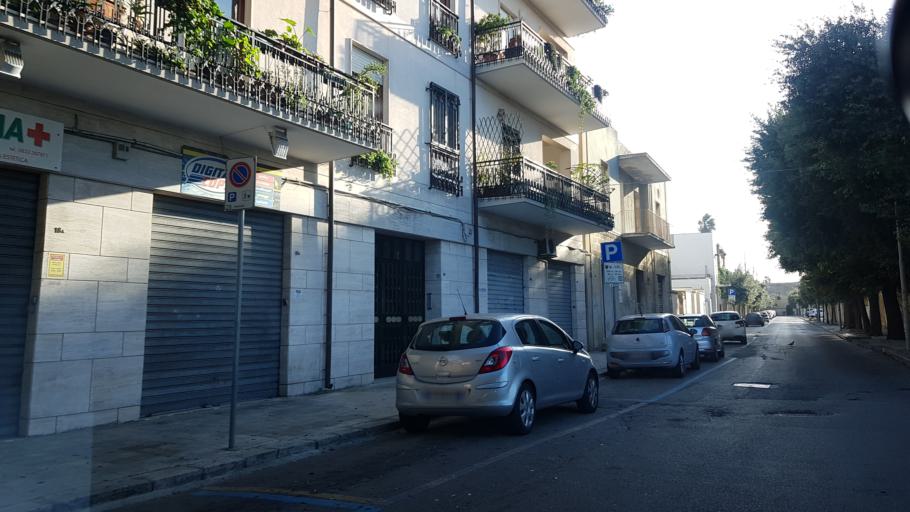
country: IT
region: Apulia
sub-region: Provincia di Lecce
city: Lecce
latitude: 40.3550
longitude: 18.1672
